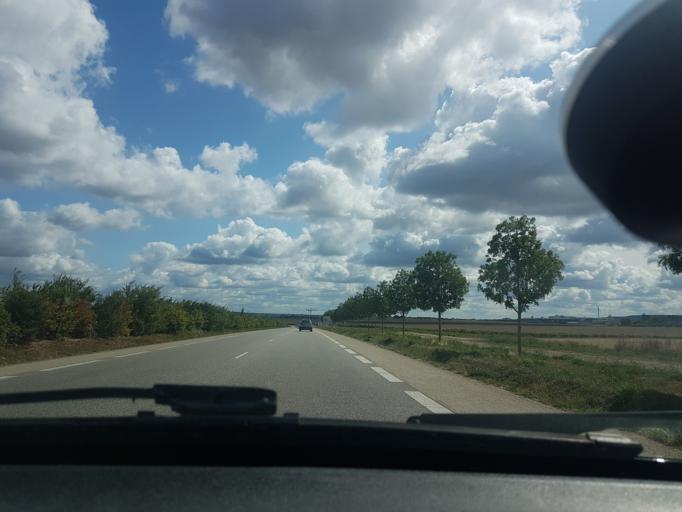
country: FR
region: Ile-de-France
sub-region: Departement des Yvelines
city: Plaisir
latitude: 48.8349
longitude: 1.9653
